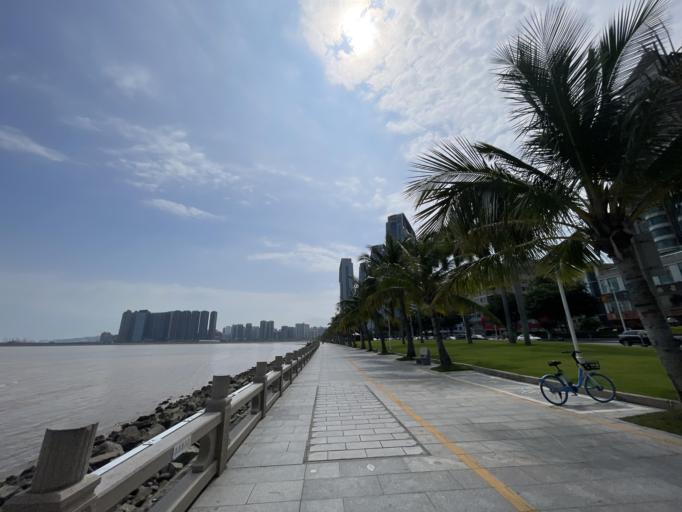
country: MO
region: Macau
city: Macau
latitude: 22.2274
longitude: 113.5577
